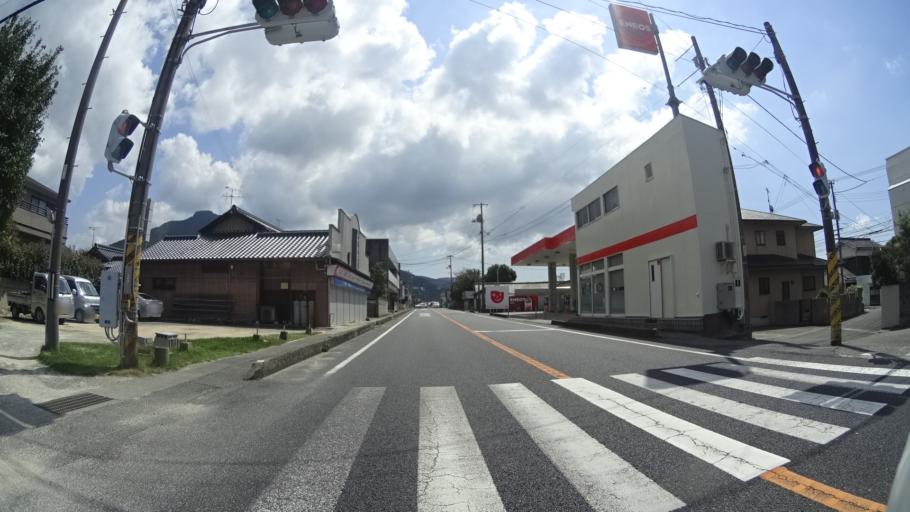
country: JP
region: Yamaguchi
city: Shimonoseki
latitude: 34.0712
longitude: 130.9002
